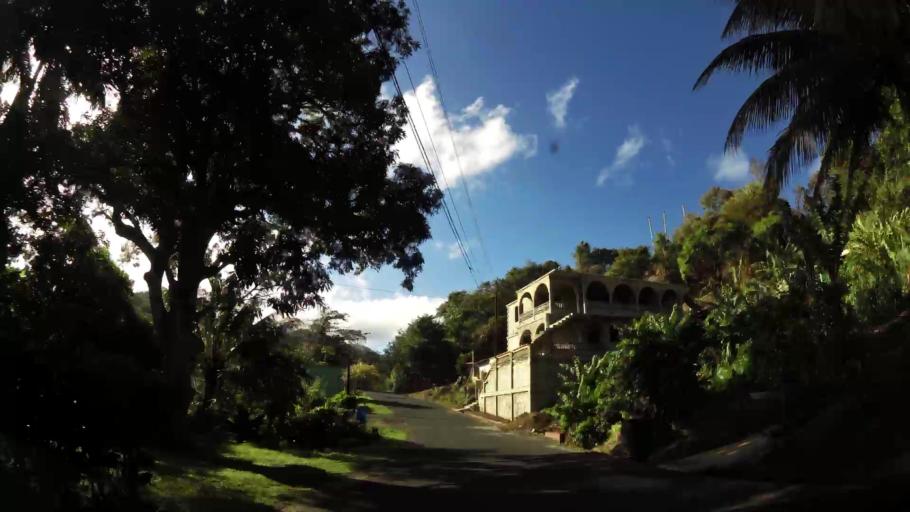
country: DM
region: Saint John
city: Portsmouth
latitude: 15.5788
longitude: -61.4196
